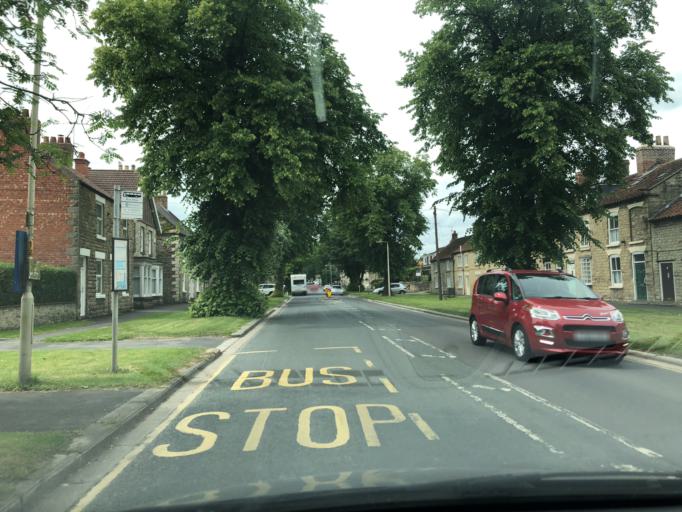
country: GB
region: England
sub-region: North Yorkshire
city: Pickering
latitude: 54.2416
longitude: -0.7695
